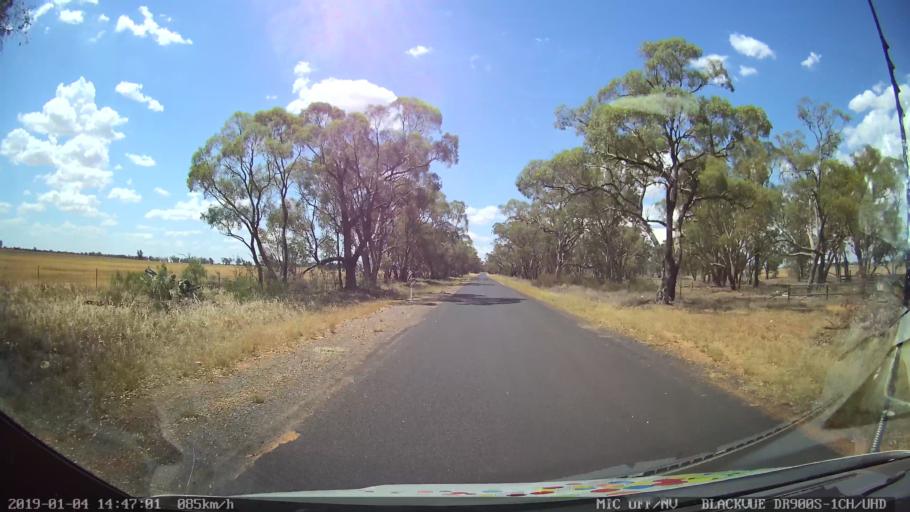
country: AU
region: New South Wales
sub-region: Dubbo Municipality
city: Dubbo
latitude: -32.0743
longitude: 148.6594
